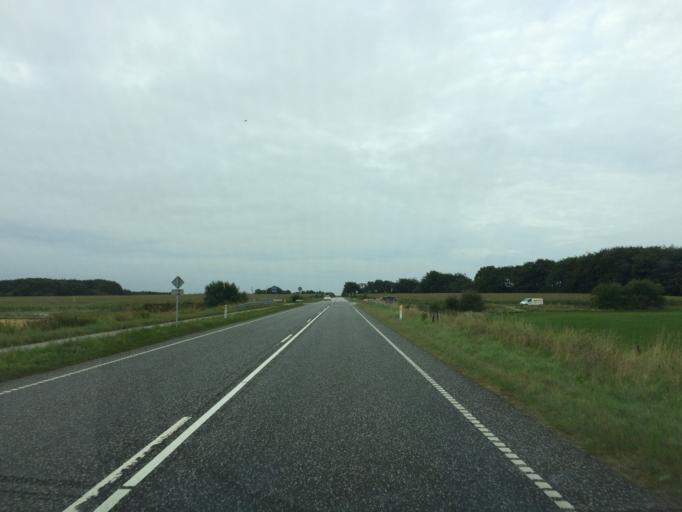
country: DK
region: Central Jutland
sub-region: Herning Kommune
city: Snejbjerg
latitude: 56.0923
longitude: 8.9260
